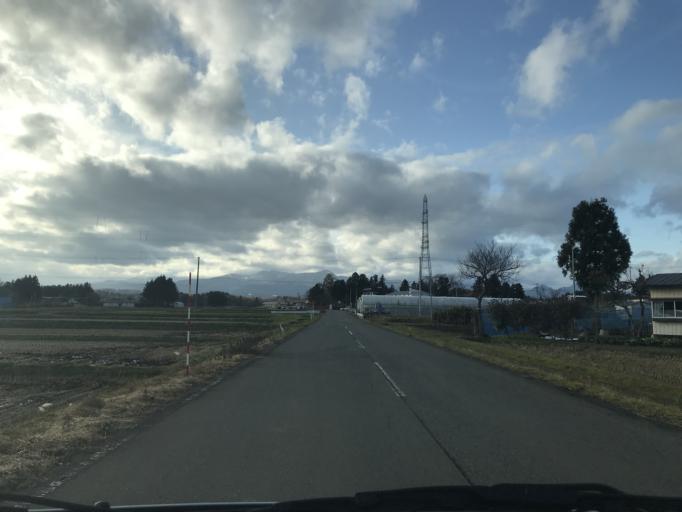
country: JP
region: Iwate
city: Mizusawa
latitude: 39.1904
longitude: 141.0830
